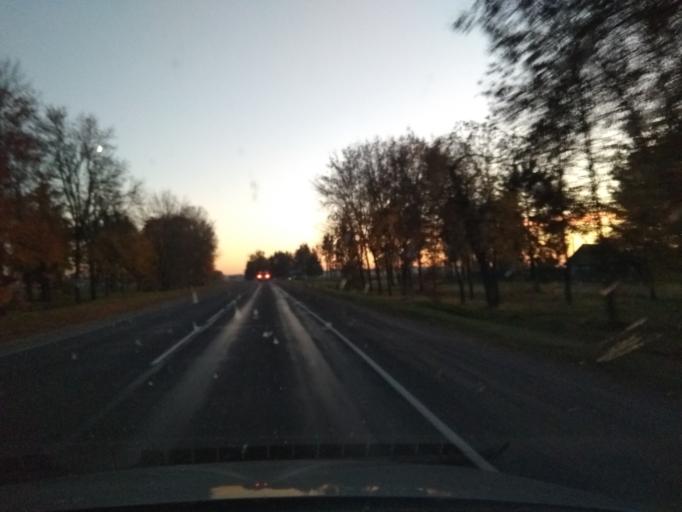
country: BY
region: Minsk
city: Dzyarzhynsk
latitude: 53.6561
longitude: 27.0782
